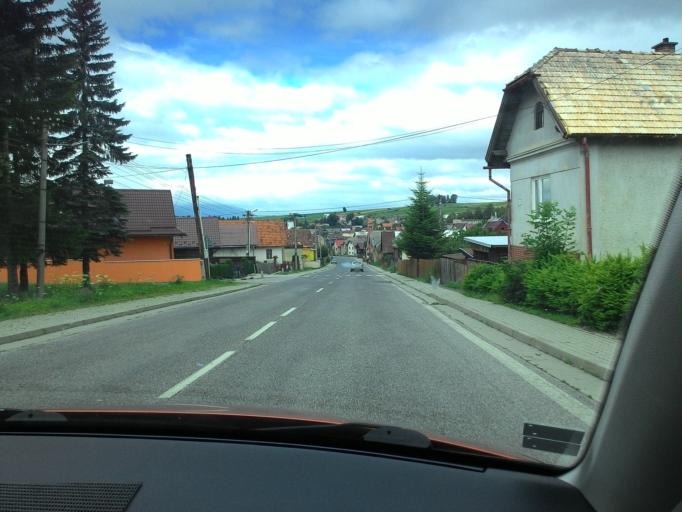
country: SK
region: Zilinsky
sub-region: Okres Liptovsky Mikulas
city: Hybe
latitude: 49.0593
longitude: 19.8953
